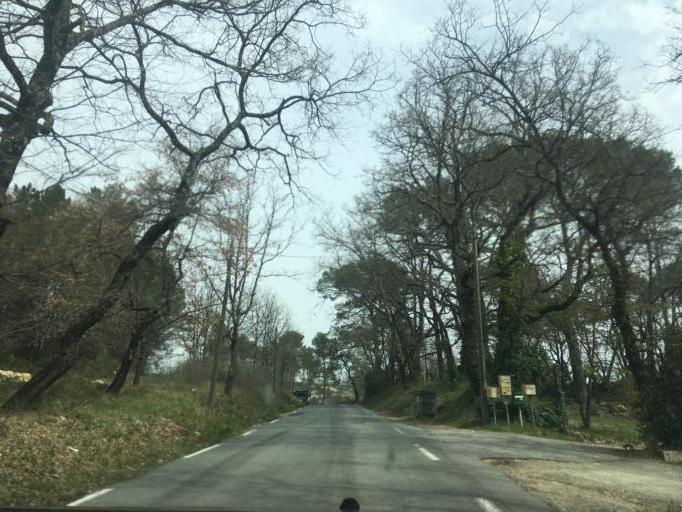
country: FR
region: Provence-Alpes-Cote d'Azur
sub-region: Departement du Var
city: Callian
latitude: 43.6026
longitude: 6.7414
